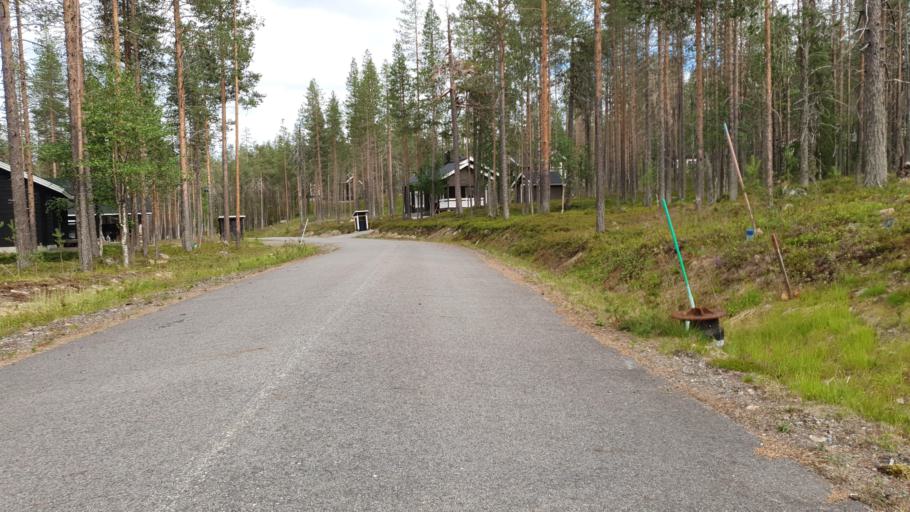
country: FI
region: Lapland
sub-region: Tunturi-Lappi
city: Kolari
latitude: 67.5906
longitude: 24.1264
